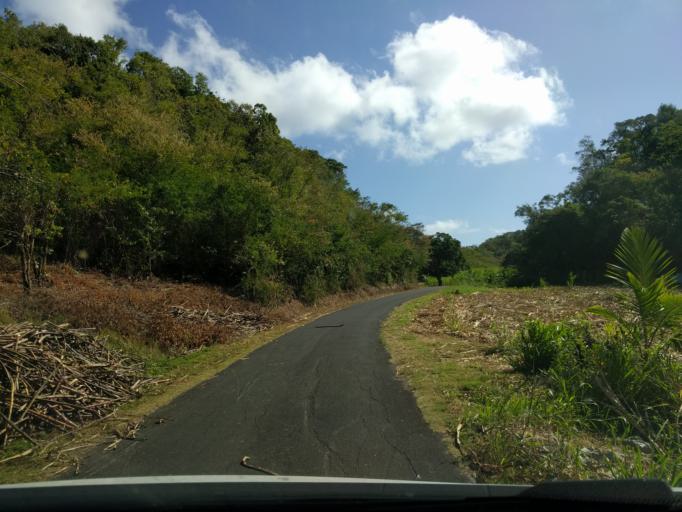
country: GP
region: Guadeloupe
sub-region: Guadeloupe
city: Grand-Bourg
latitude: 15.9723
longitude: -61.2621
